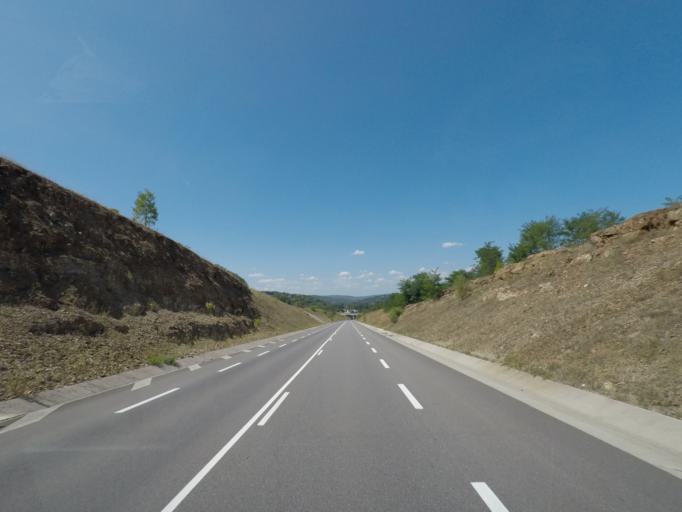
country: FR
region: Midi-Pyrenees
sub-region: Departement du Lot
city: Figeac
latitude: 44.5879
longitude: 2.0034
